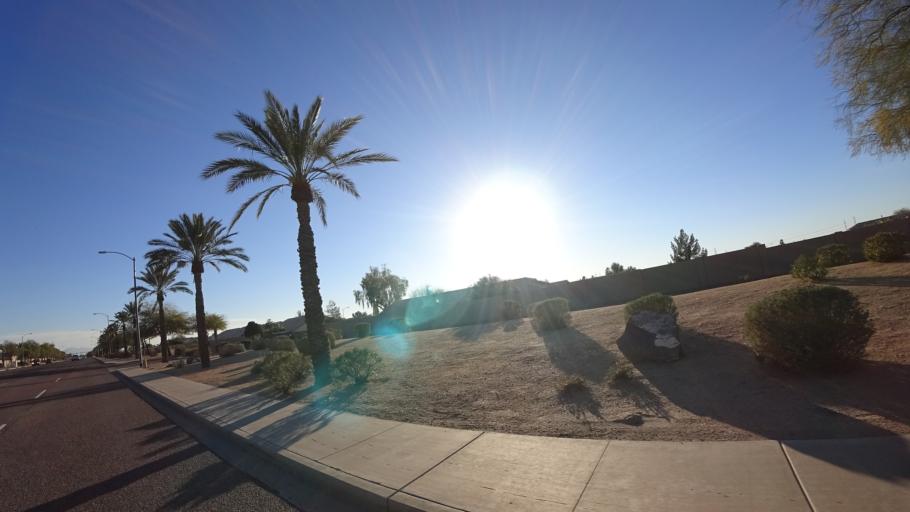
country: US
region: Arizona
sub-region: Maricopa County
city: Sun City West
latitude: 33.6720
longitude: -112.2900
